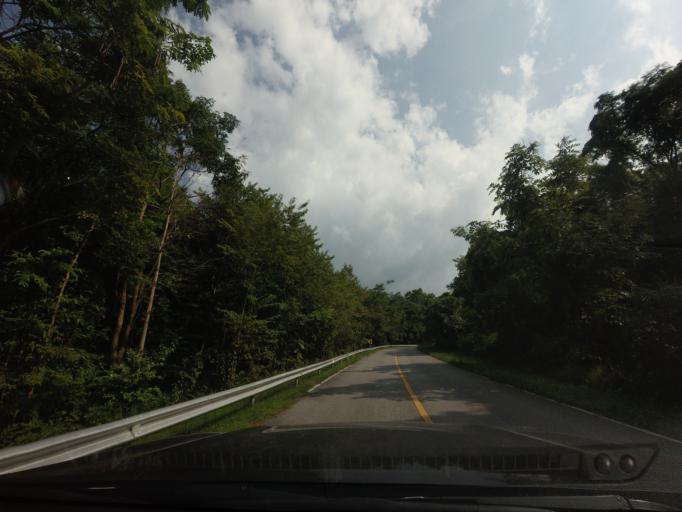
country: TH
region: Phitsanulok
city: Nakhon Thai
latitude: 17.0197
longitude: 100.9583
